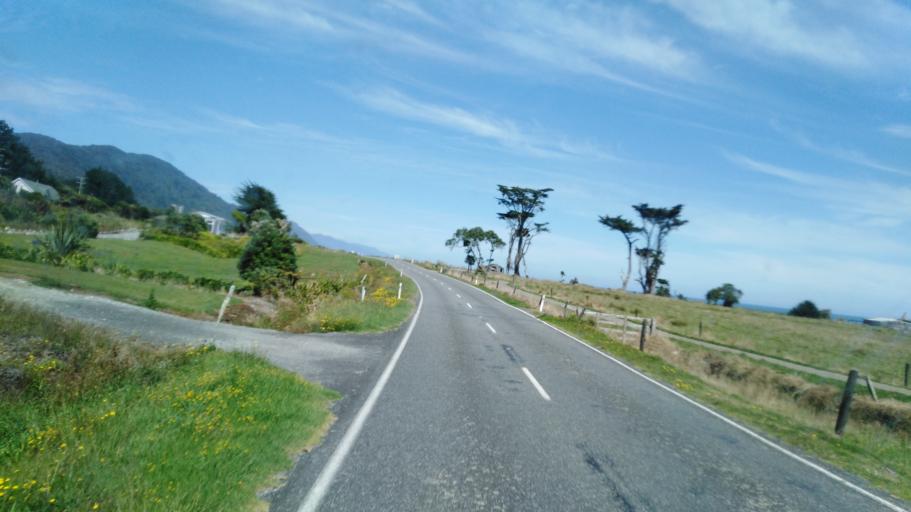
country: NZ
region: West Coast
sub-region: Buller District
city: Westport
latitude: -41.5374
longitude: 171.9302
